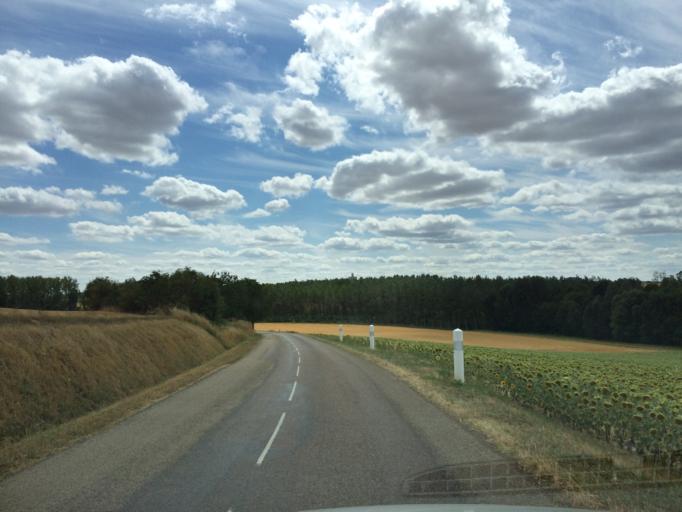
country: FR
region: Bourgogne
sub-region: Departement de l'Yonne
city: Laroche-Saint-Cydroine
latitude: 47.9293
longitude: 3.4450
